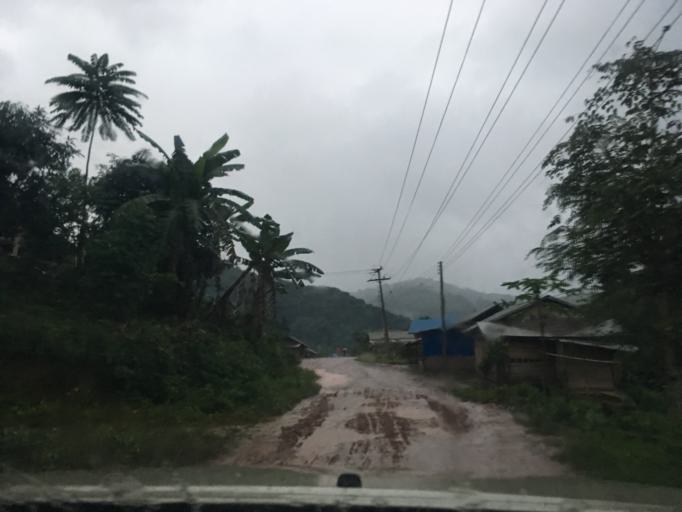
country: LA
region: Oudomxai
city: Muang La
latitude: 21.2579
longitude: 101.9303
